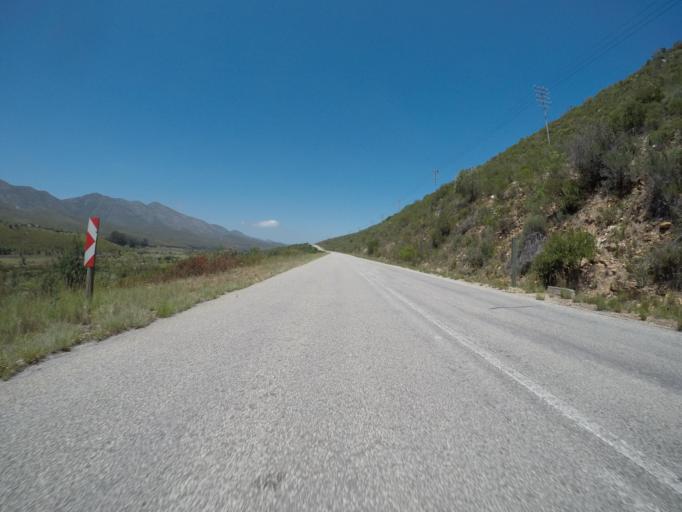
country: ZA
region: Eastern Cape
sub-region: Cacadu District Municipality
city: Kareedouw
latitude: -33.9050
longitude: 24.1393
